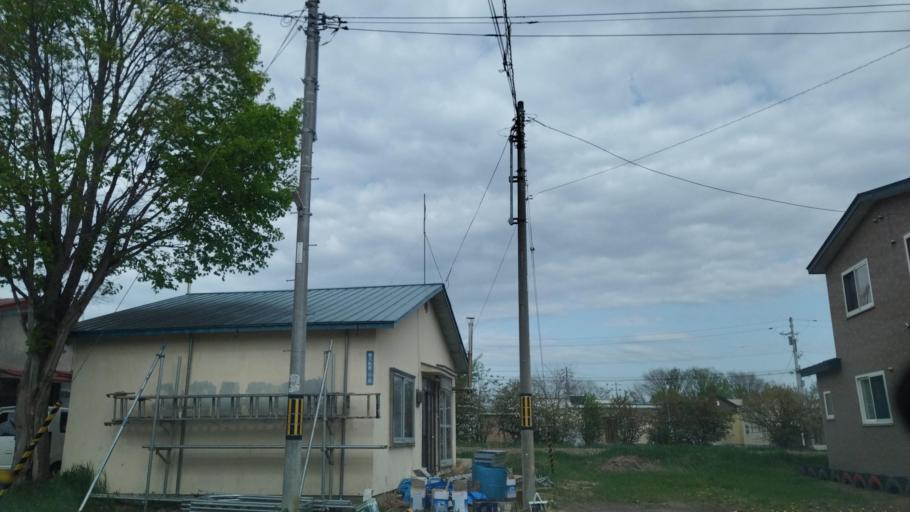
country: JP
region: Hokkaido
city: Obihiro
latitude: 42.9307
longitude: 143.2167
